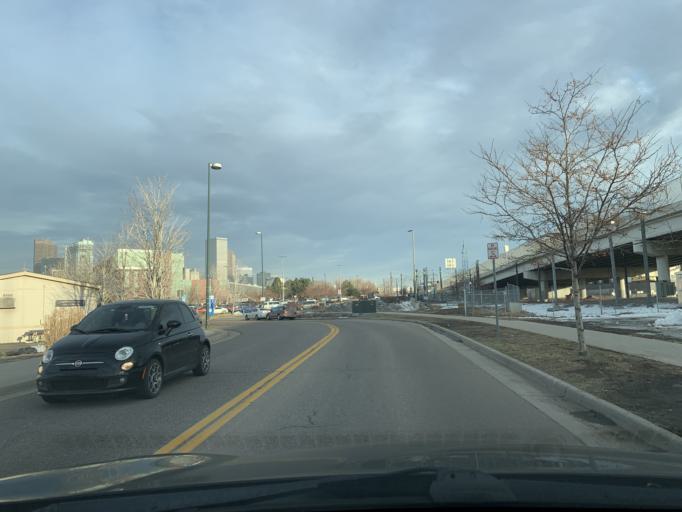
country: US
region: Colorado
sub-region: Denver County
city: Denver
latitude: 39.7407
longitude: -105.0079
